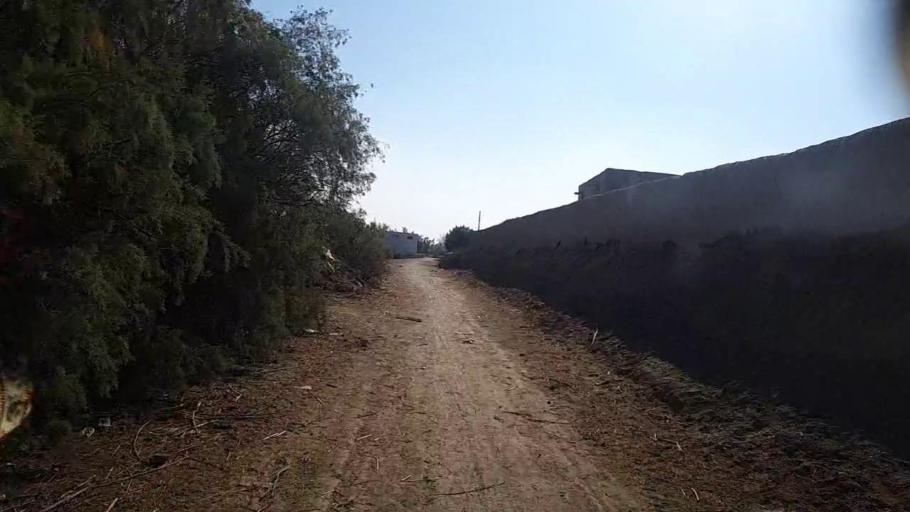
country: PK
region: Sindh
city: Khairpur
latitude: 27.9481
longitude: 69.7505
